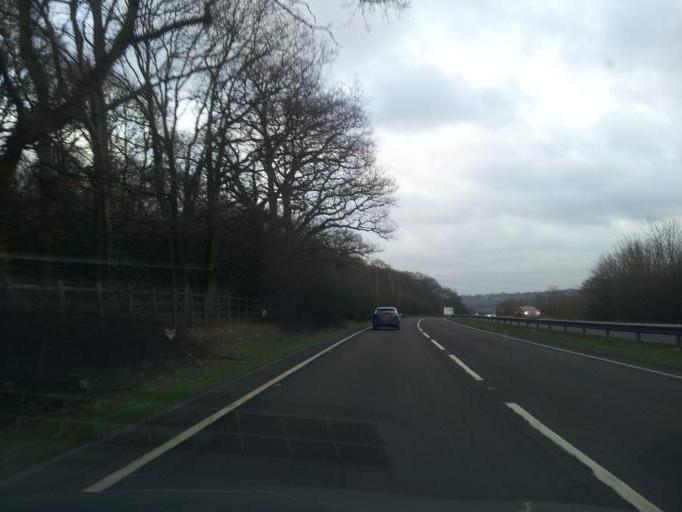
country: GB
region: England
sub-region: Hertfordshire
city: Berkhamsted
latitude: 51.7485
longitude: -0.5536
